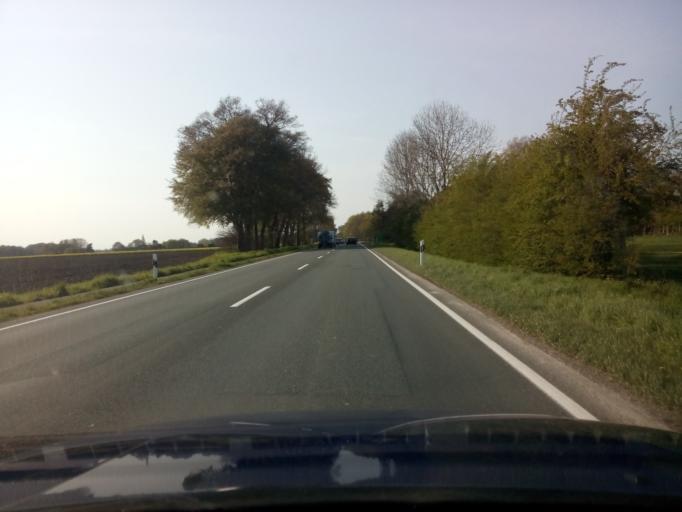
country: DE
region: Lower Saxony
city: Sustedt
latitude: 52.8551
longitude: 8.8889
